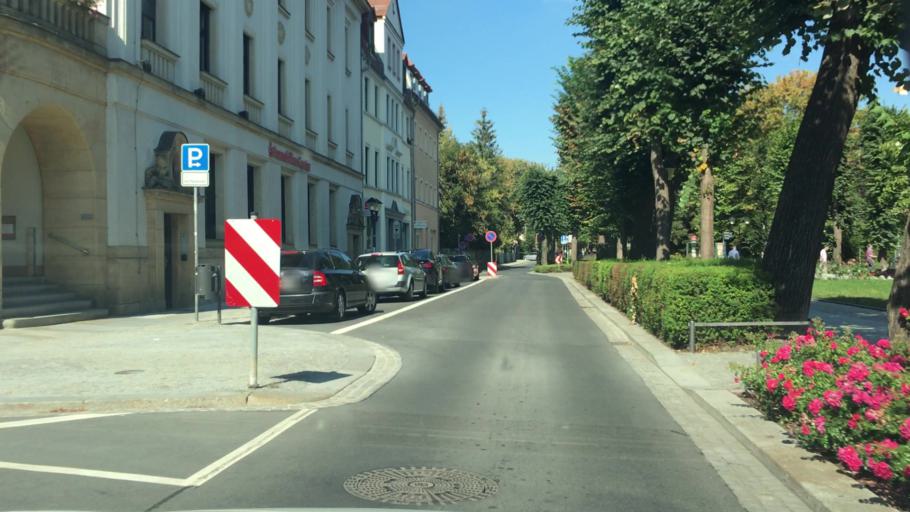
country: DE
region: Saxony
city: Pirna
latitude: 50.9620
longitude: 13.9379
